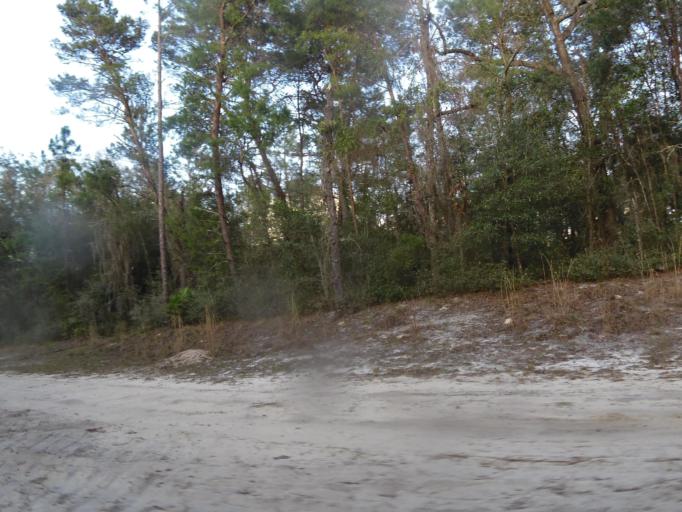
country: US
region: Florida
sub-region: Putnam County
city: Interlachen
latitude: 29.7816
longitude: -81.8395
